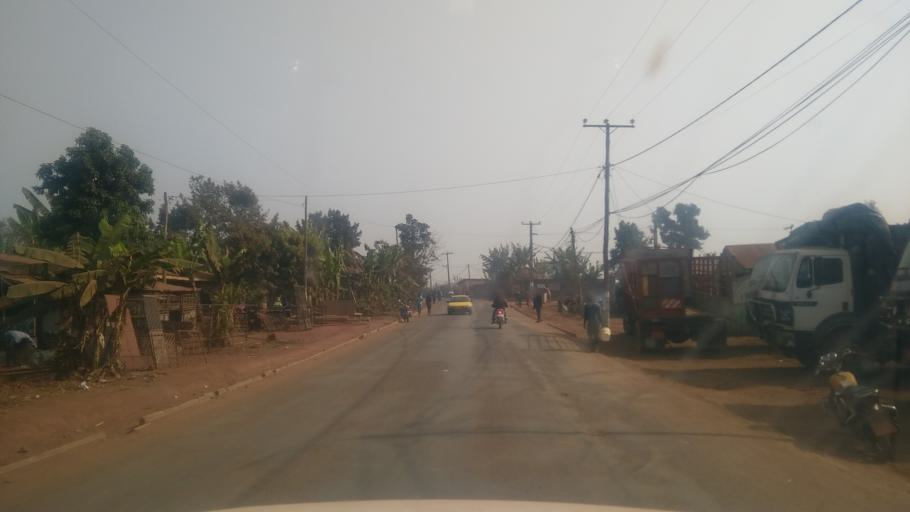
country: CM
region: West
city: Bafoussam
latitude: 5.5009
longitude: 10.3974
